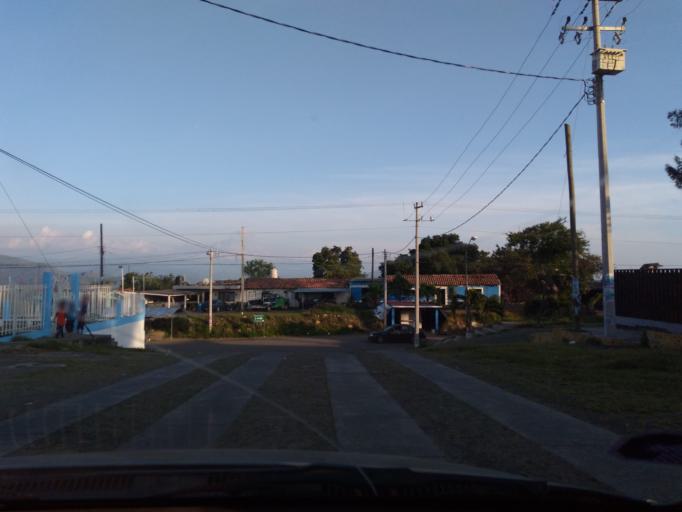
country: MX
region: Jalisco
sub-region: Tonila
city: San Marcos
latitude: 19.4451
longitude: -103.5062
